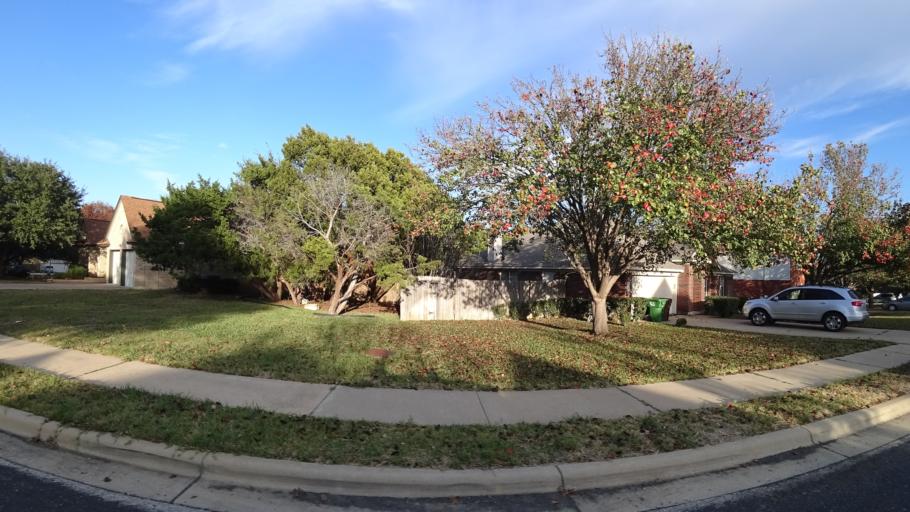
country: US
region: Texas
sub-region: Williamson County
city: Brushy Creek
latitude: 30.5034
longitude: -97.7361
